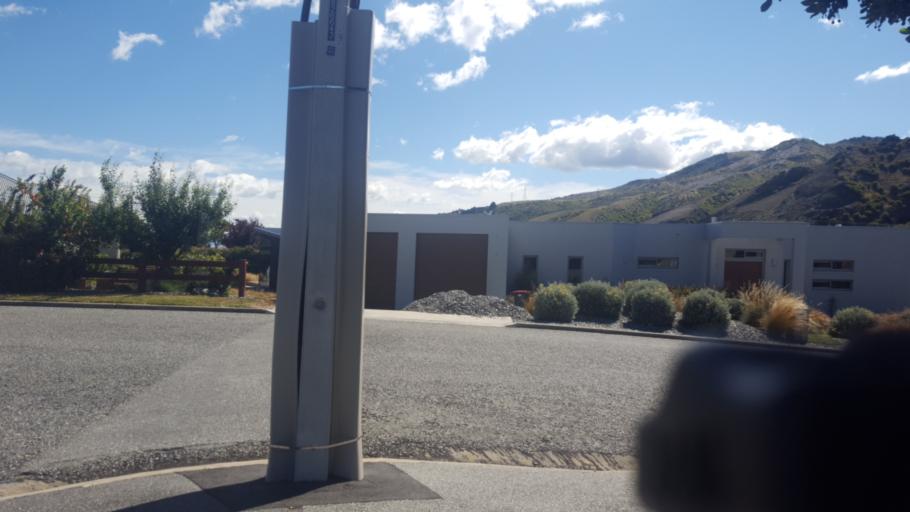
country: NZ
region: Otago
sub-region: Queenstown-Lakes District
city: Wanaka
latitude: -45.0485
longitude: 169.2111
